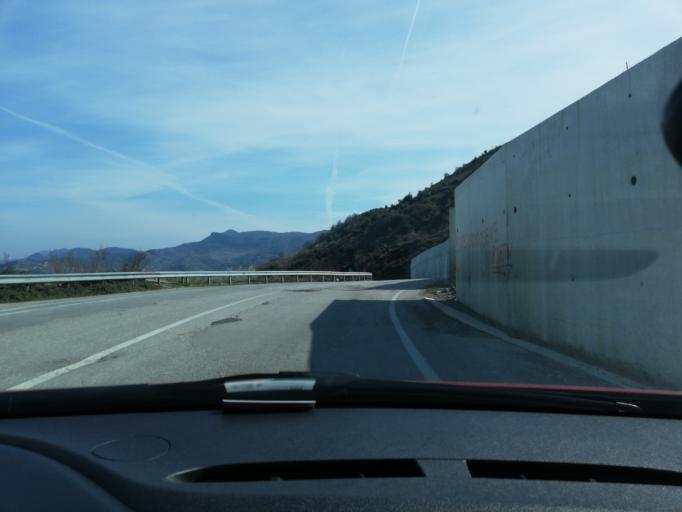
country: TR
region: Bartin
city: Kurucasile
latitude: 41.8275
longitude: 32.6483
